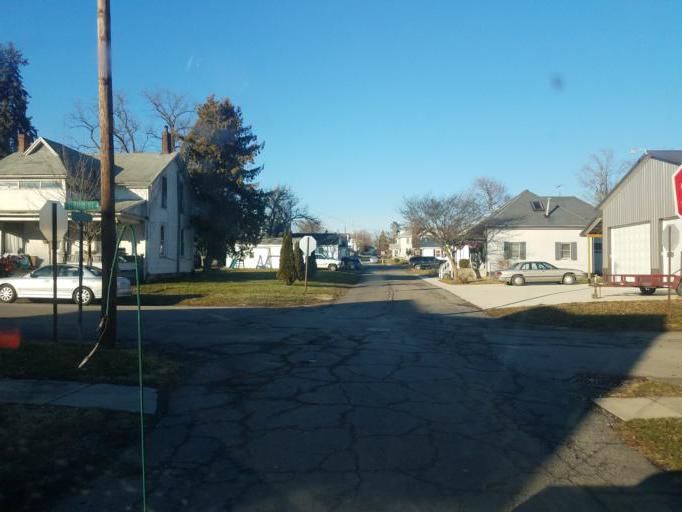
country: US
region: Ohio
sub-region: Hardin County
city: Kenton
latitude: 40.6457
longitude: -83.6024
